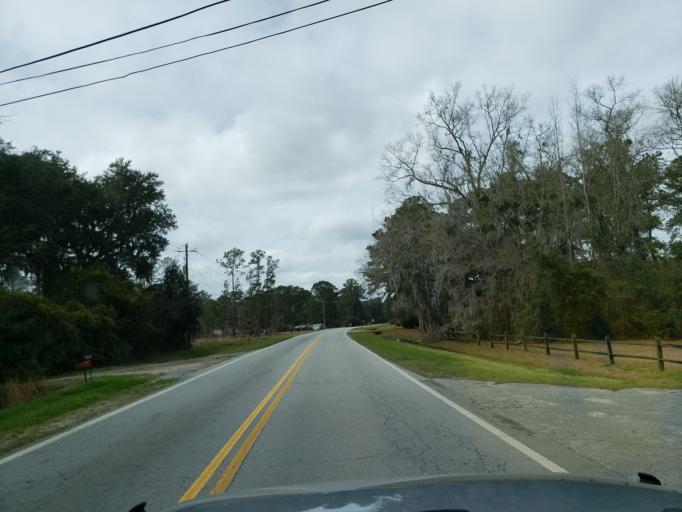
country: US
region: Georgia
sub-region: Chatham County
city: Pooler
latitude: 32.0467
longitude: -81.2831
